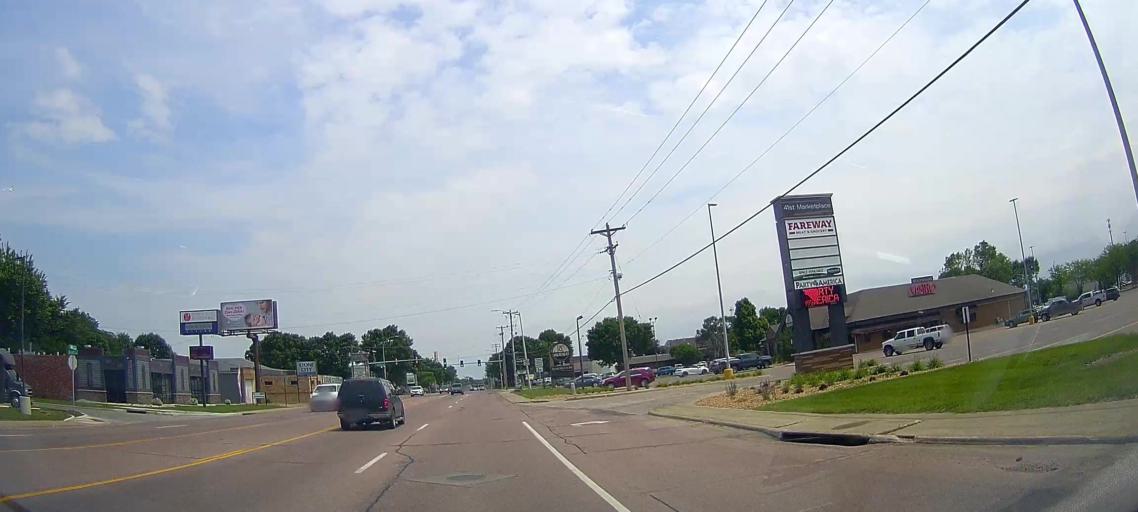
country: US
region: South Dakota
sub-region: Minnehaha County
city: Sioux Falls
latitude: 43.5148
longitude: -96.7425
